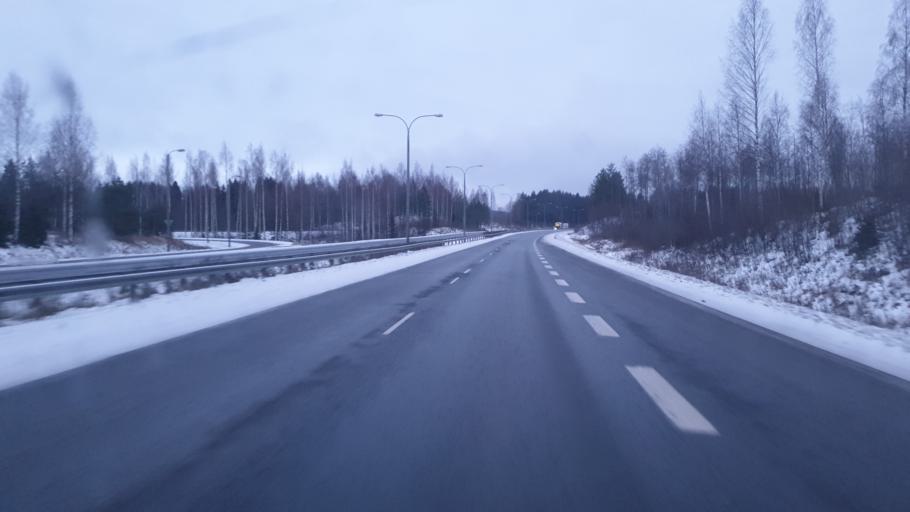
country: FI
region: Northern Savo
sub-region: Kuopio
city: Siilinjaervi
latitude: 63.0586
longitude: 27.6713
